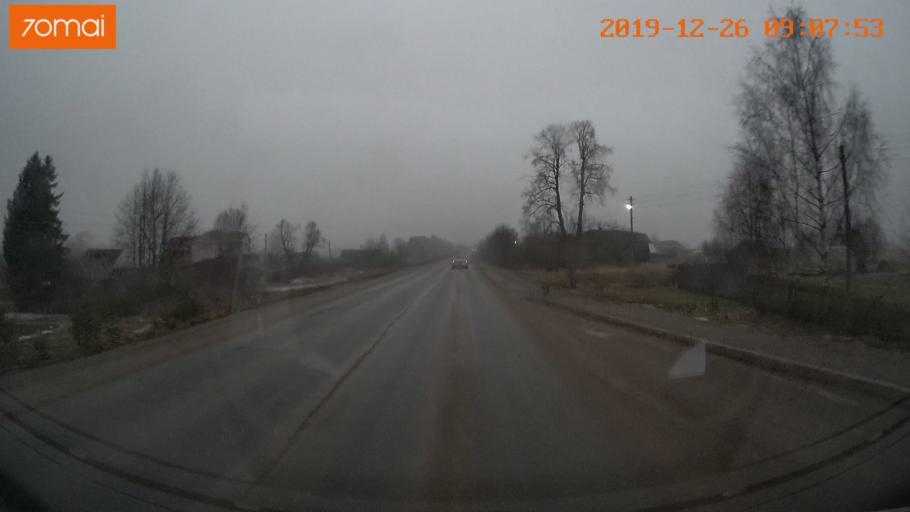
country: RU
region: Vologda
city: Gryazovets
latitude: 58.8508
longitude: 40.2469
